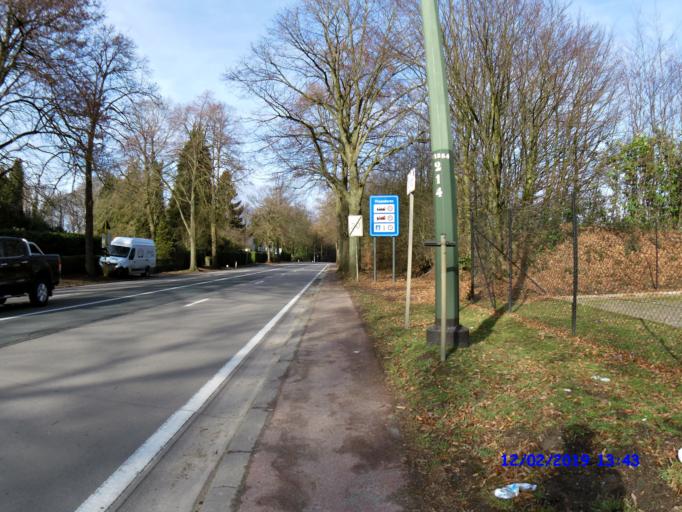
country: BE
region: Wallonia
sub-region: Province du Brabant Wallon
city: Waterloo
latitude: 50.7359
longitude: 4.3955
